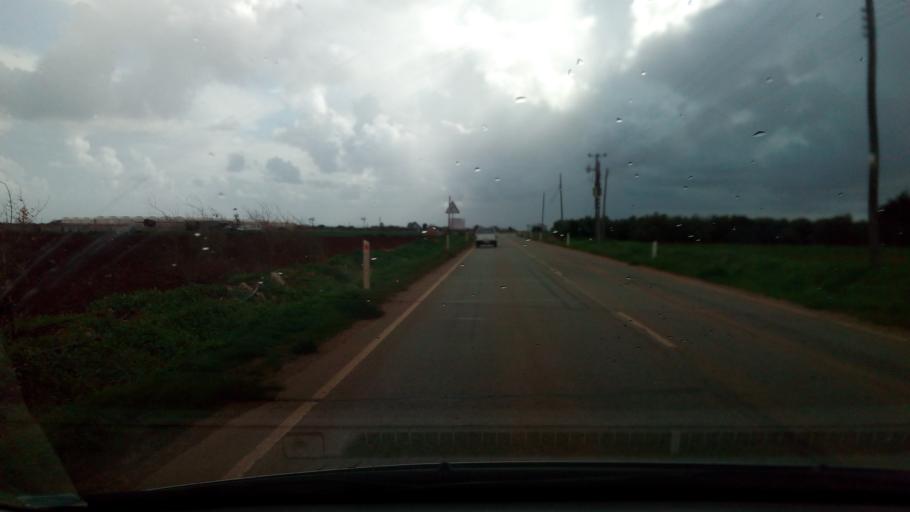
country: CY
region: Ammochostos
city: Liopetri
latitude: 34.9877
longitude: 33.8937
